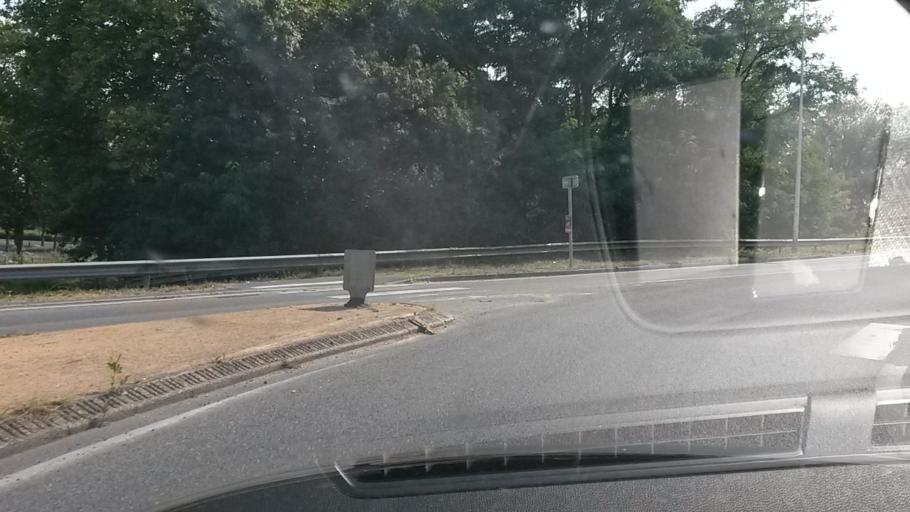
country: FR
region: Pays de la Loire
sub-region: Departement de la Loire-Atlantique
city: Ancenis
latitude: 47.3723
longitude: -1.1675
